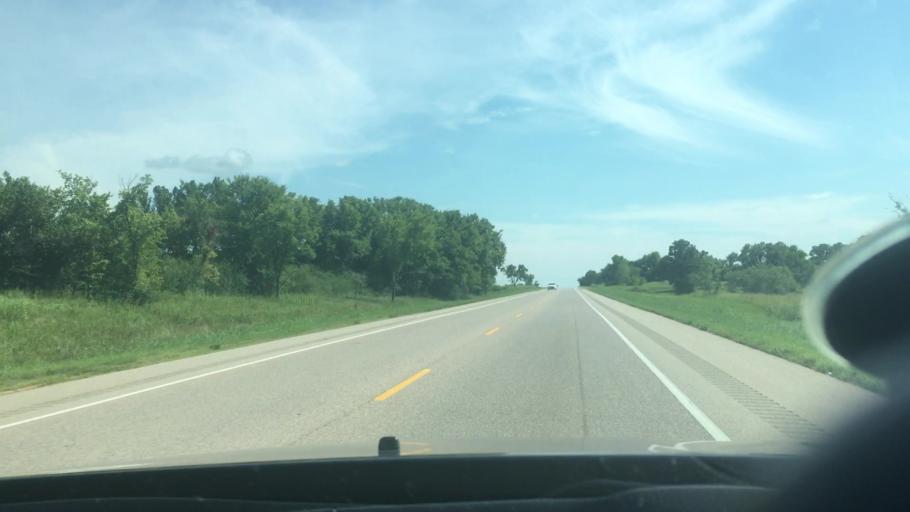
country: US
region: Oklahoma
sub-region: Seminole County
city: Seminole
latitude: 35.1621
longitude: -96.6742
